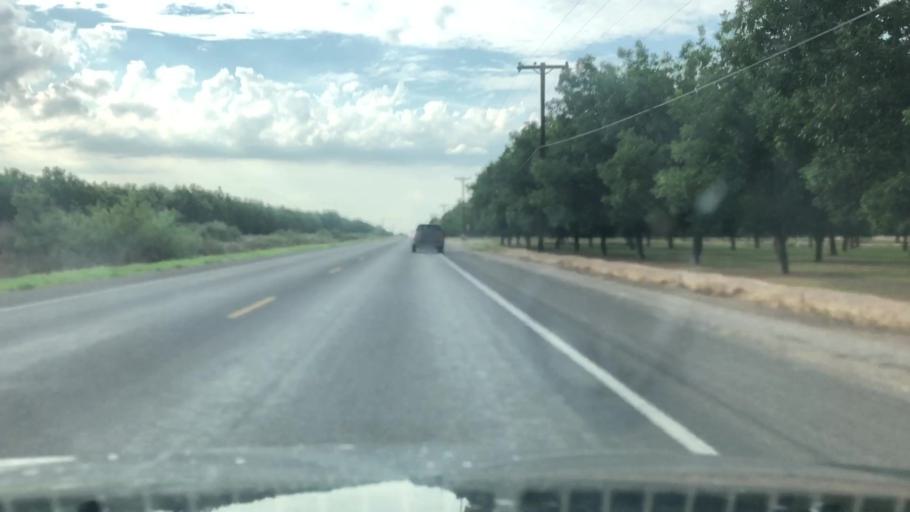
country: US
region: New Mexico
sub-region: Dona Ana County
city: Mesquite
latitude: 32.2130
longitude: -106.7271
